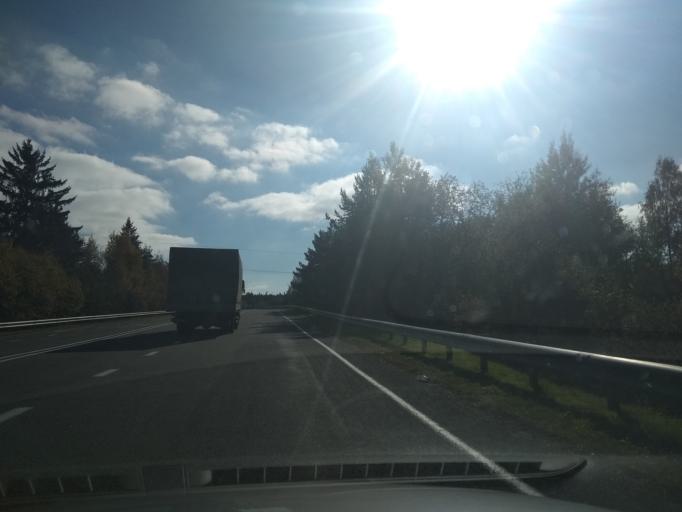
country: BY
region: Minsk
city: Haradzyeya
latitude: 53.3835
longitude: 26.5076
